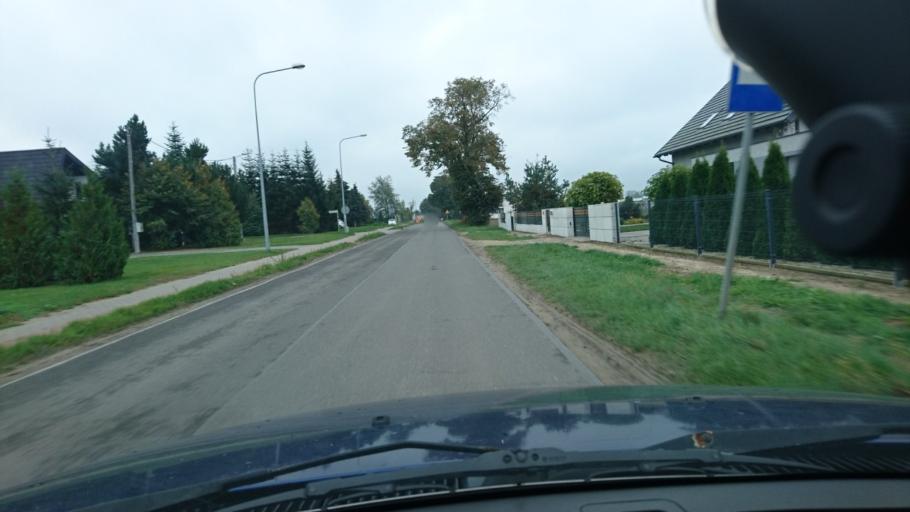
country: PL
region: Greater Poland Voivodeship
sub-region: Powiat ostrowski
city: Odolanow
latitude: 51.5765
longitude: 17.6541
